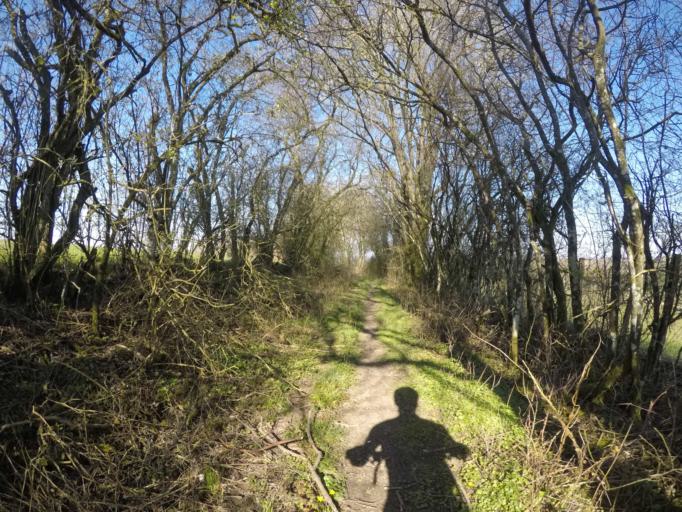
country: BE
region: Wallonia
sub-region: Province du Luxembourg
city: Tintigny
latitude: 49.7064
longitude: 5.5569
